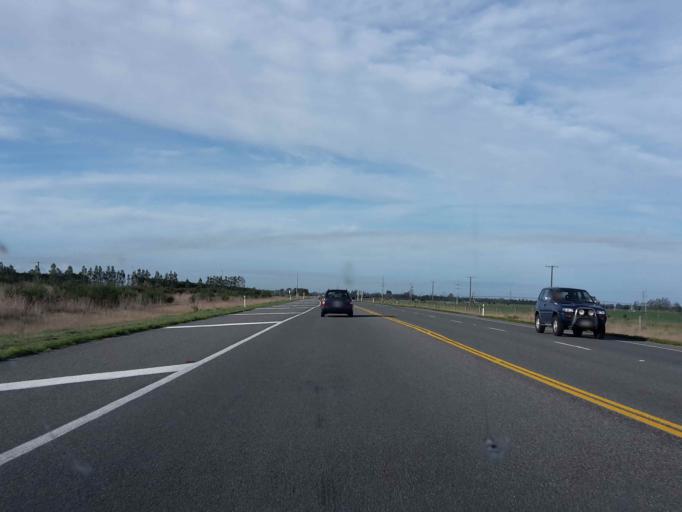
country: NZ
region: Canterbury
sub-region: Ashburton District
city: Tinwald
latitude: -44.0196
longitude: 171.5189
